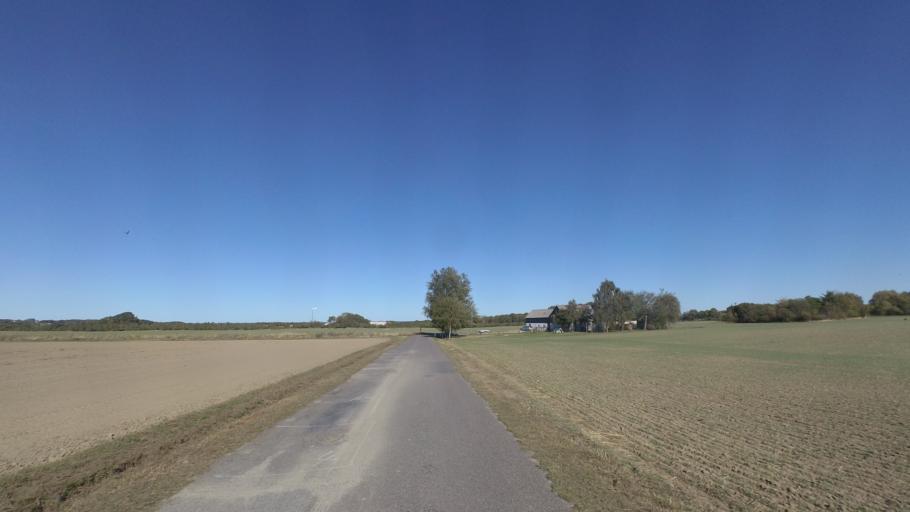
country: DK
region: Capital Region
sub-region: Bornholm Kommune
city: Nexo
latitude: 55.1200
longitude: 15.0478
